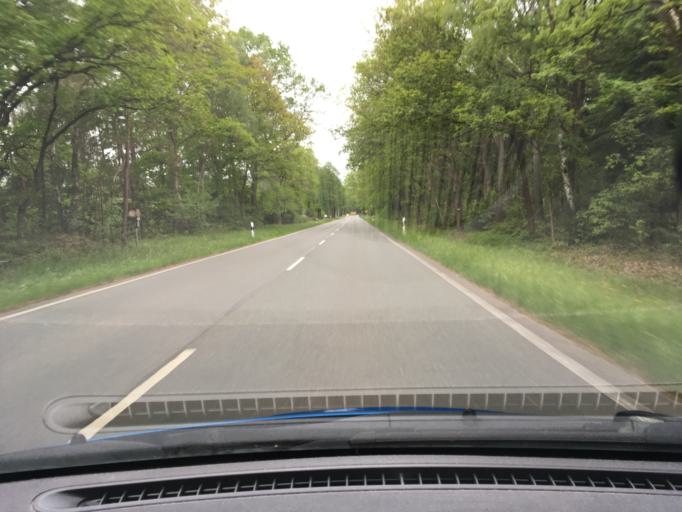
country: DE
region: Lower Saxony
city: Bispingen
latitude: 53.0937
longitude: 10.0344
